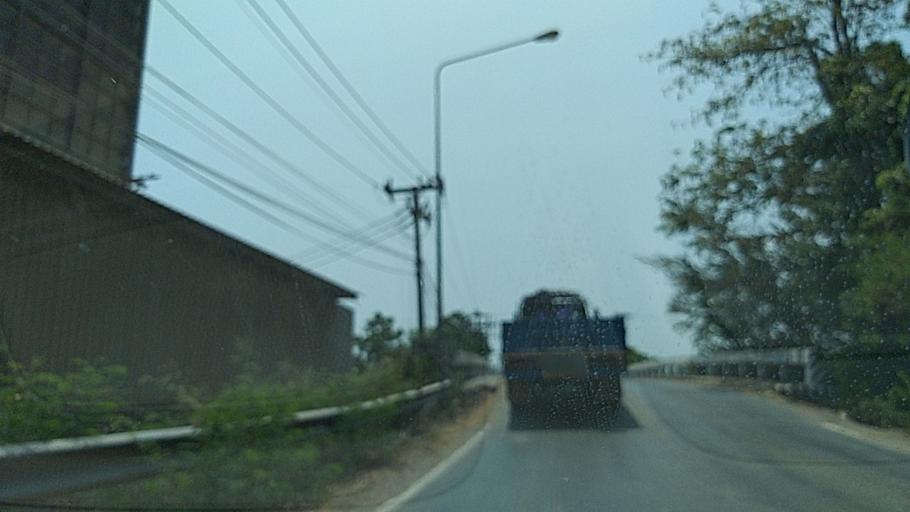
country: TH
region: Chachoengsao
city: Bang Nam Priao
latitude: 13.9688
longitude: 100.9663
